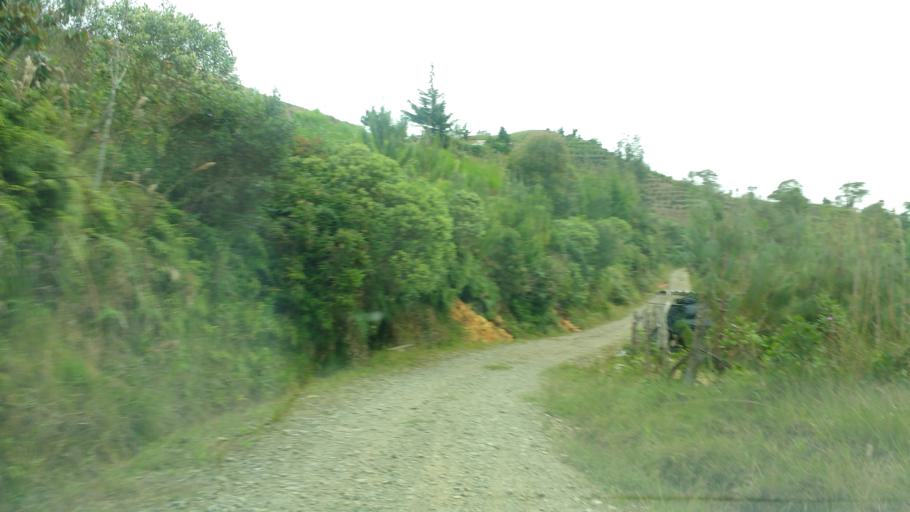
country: CO
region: Antioquia
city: Concepcion
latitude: 6.3686
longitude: -75.2258
